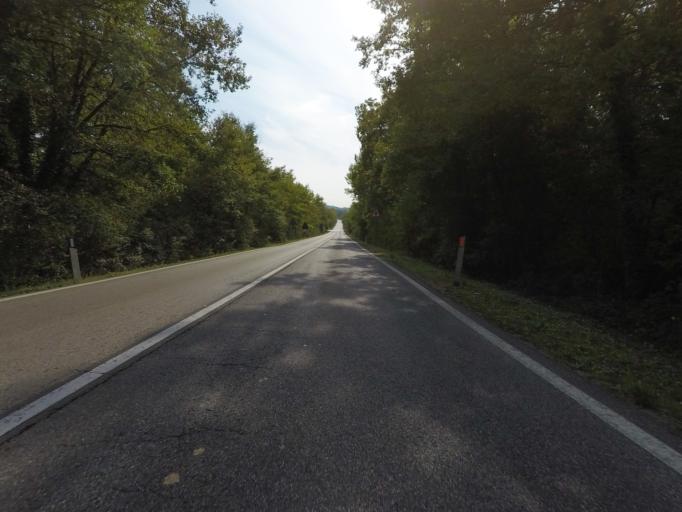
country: IT
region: Tuscany
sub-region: Provincia di Siena
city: Rosia
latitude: 43.1776
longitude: 11.2780
